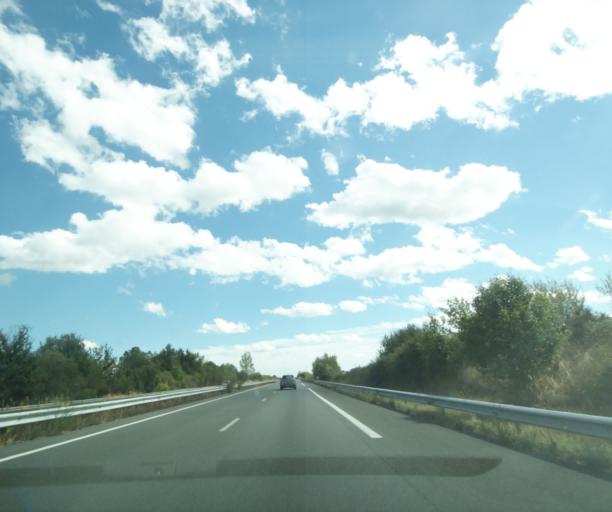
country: FR
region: Aquitaine
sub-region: Departement du Lot-et-Garonne
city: Fourques-sur-Garonne
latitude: 44.4471
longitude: 0.0999
